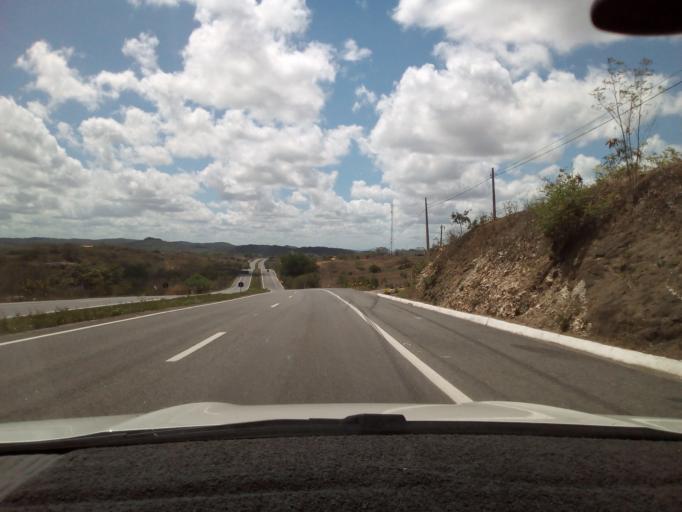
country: BR
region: Paraiba
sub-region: Campina Grande
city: Campina Grande
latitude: -7.2550
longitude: -35.8273
